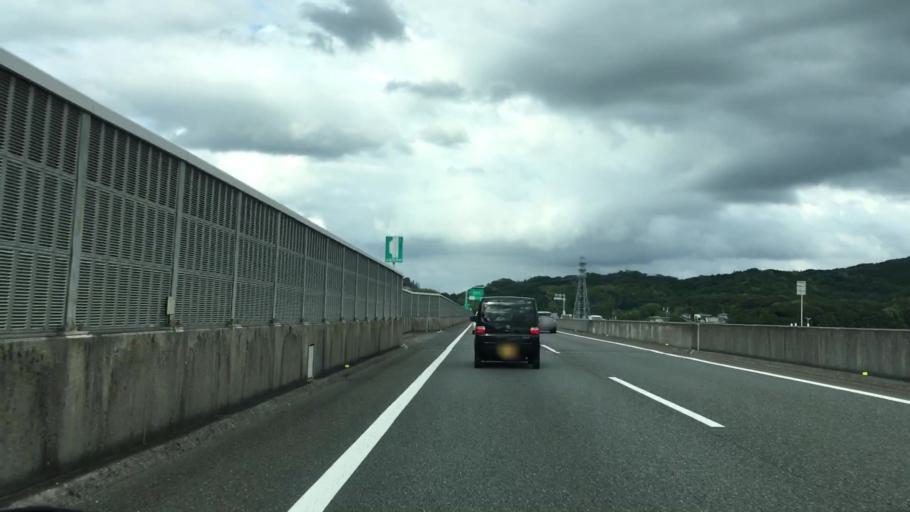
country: JP
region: Fukuoka
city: Maebaru-chuo
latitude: 33.5646
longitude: 130.2388
